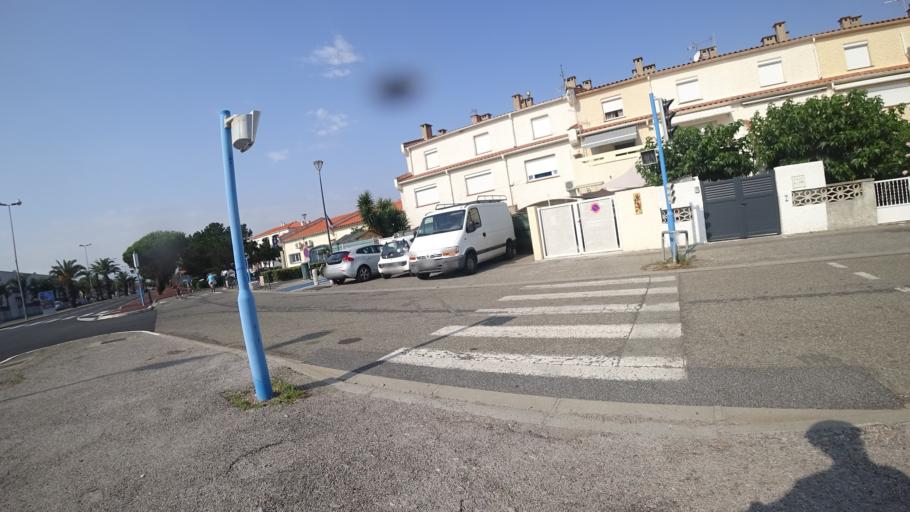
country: FR
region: Languedoc-Roussillon
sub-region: Departement des Pyrenees-Orientales
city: Saint-Cyprien-Plage
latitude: 42.6335
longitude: 3.0327
